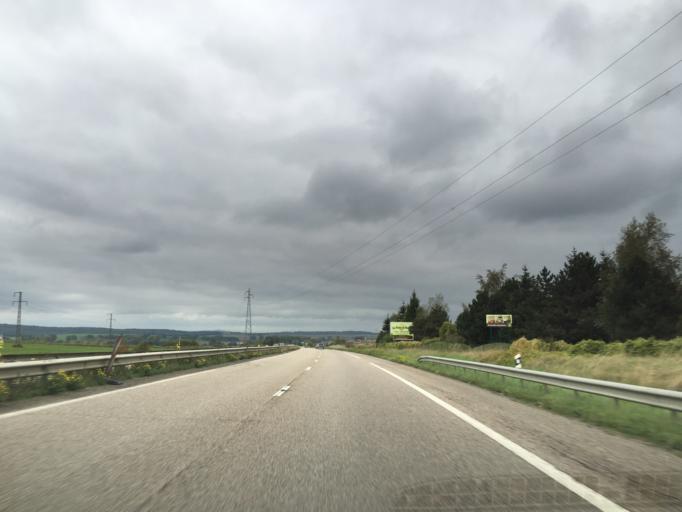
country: FR
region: Lorraine
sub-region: Departement de Meurthe-et-Moselle
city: Foug
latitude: 48.6815
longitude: 5.7437
